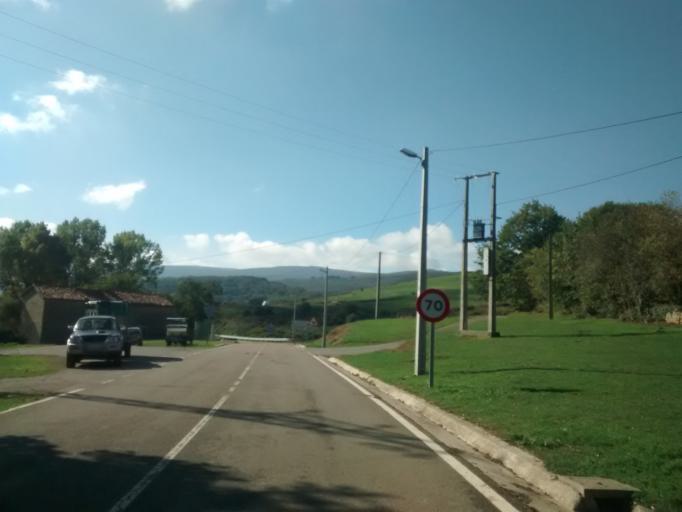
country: ES
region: Cantabria
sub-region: Provincia de Cantabria
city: Reinosa
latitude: 42.9685
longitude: -4.0609
